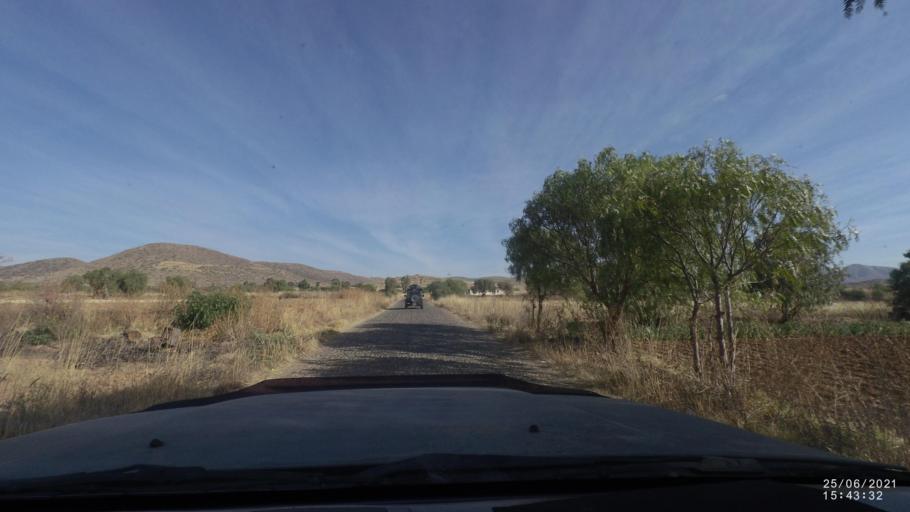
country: BO
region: Cochabamba
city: Cliza
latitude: -17.6493
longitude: -65.9125
